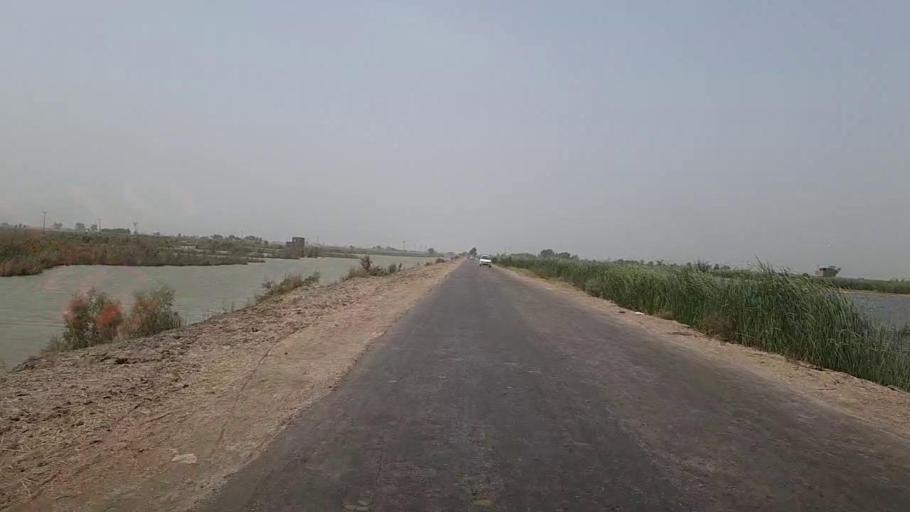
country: PK
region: Sindh
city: Radhan
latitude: 27.1519
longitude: 67.9390
